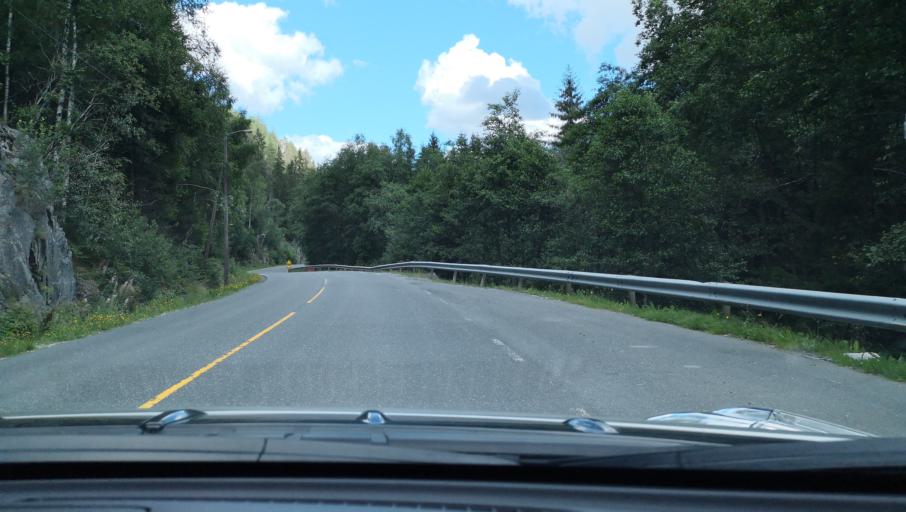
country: NO
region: Ostfold
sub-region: Hobol
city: Tomter
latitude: 59.6485
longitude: 10.9909
